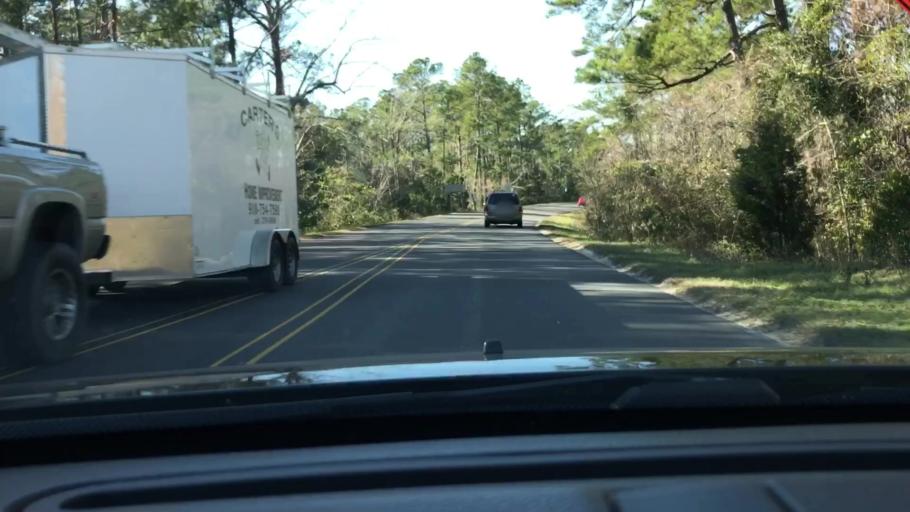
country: US
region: North Carolina
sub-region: Brunswick County
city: Shallotte
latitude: 33.9692
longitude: -78.3921
